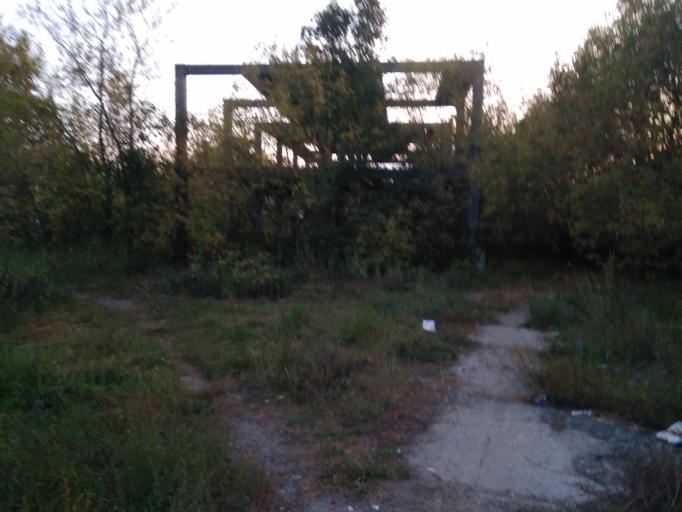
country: RU
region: Moskovskaya
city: Zhukovskiy
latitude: 55.5999
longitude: 38.1028
